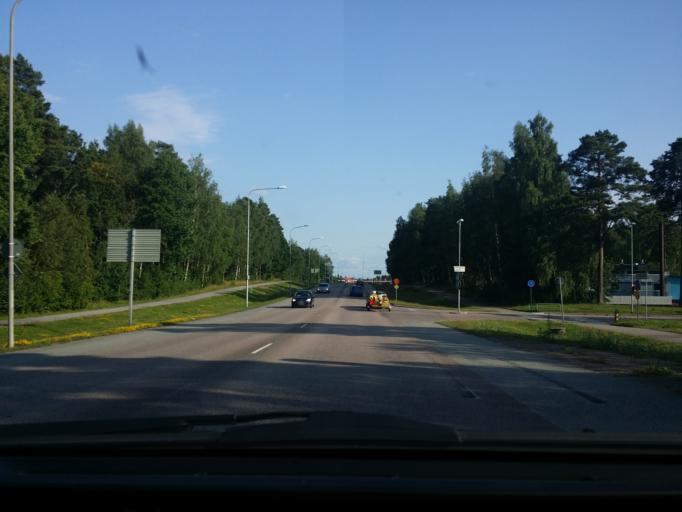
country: SE
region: Vaestmanland
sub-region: Vasteras
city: Vasteras
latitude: 59.6199
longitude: 16.6002
